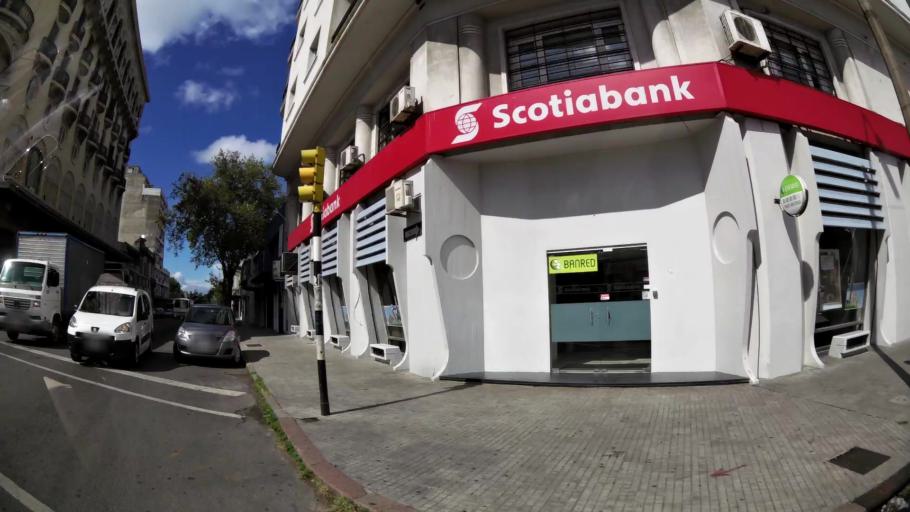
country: UY
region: Montevideo
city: Montevideo
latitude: -34.8896
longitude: -56.1876
